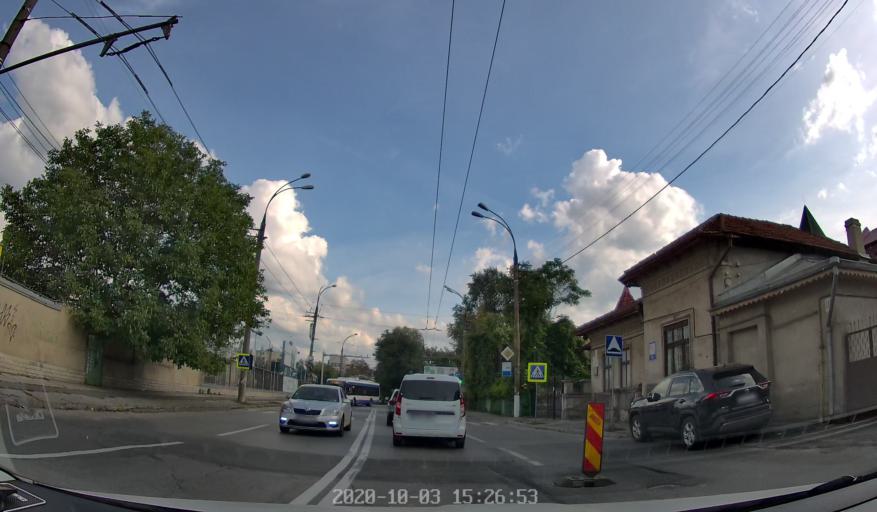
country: MD
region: Chisinau
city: Chisinau
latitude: 47.0267
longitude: 28.8176
